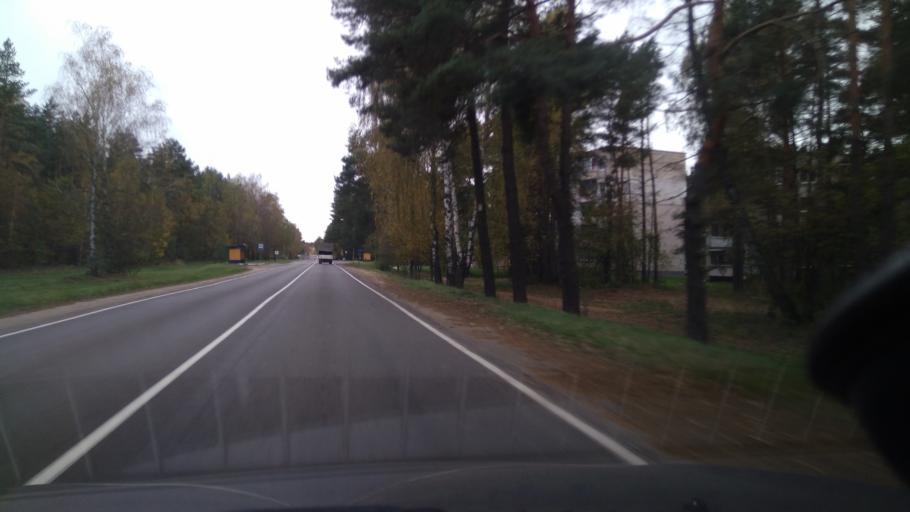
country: BY
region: Minsk
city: Svislach
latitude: 53.6489
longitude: 27.9240
